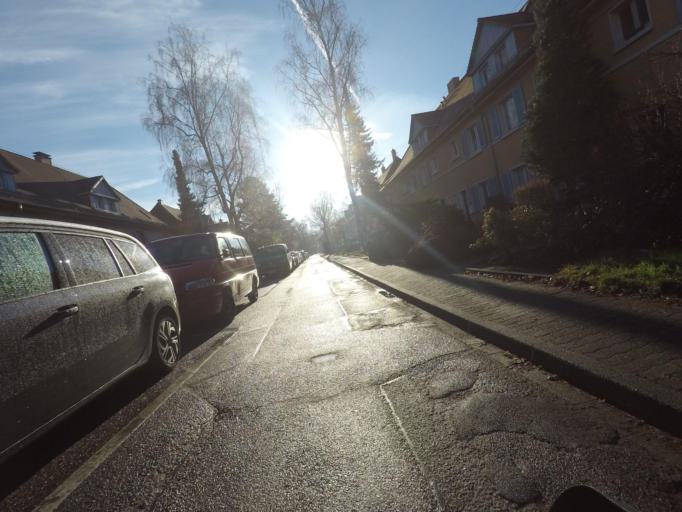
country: DE
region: Baden-Wuerttemberg
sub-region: Karlsruhe Region
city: Karlsruhe
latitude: 48.9763
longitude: 8.4110
